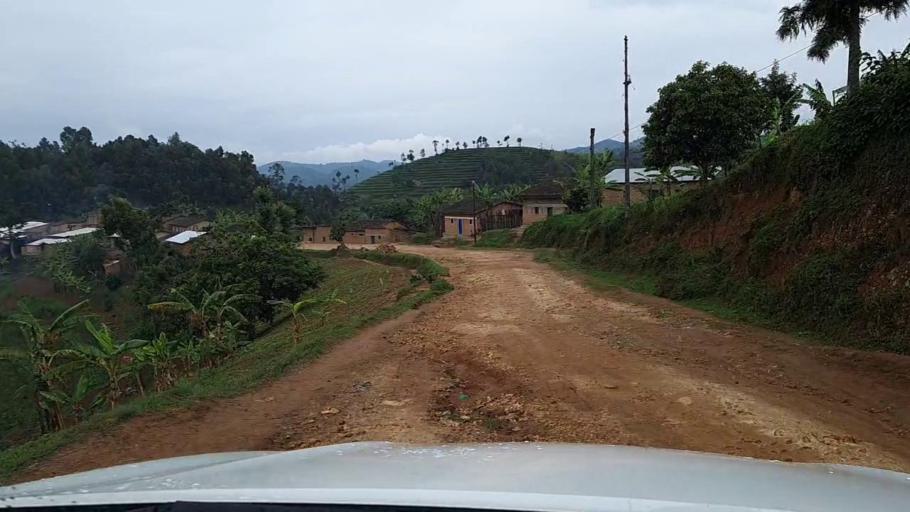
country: RW
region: Southern Province
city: Nzega
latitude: -2.4556
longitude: 29.4697
